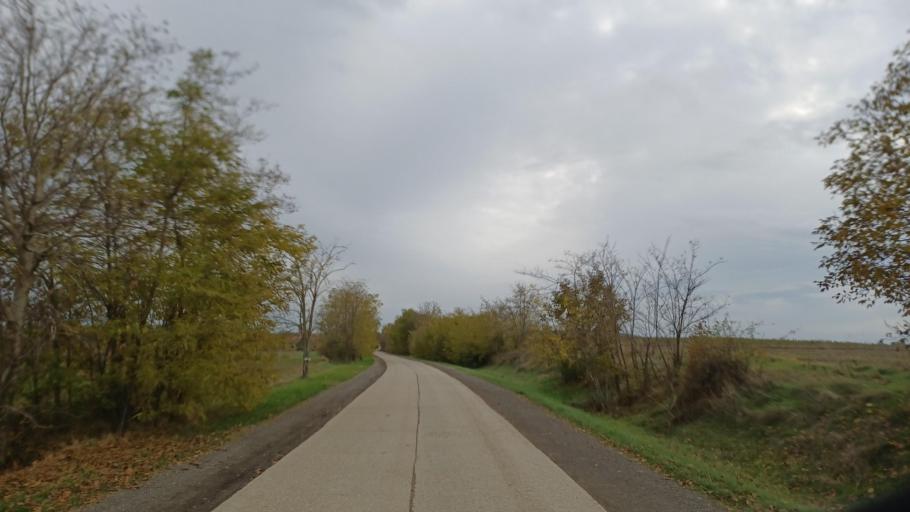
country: HU
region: Tolna
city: Nagydorog
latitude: 46.6348
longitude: 18.6046
